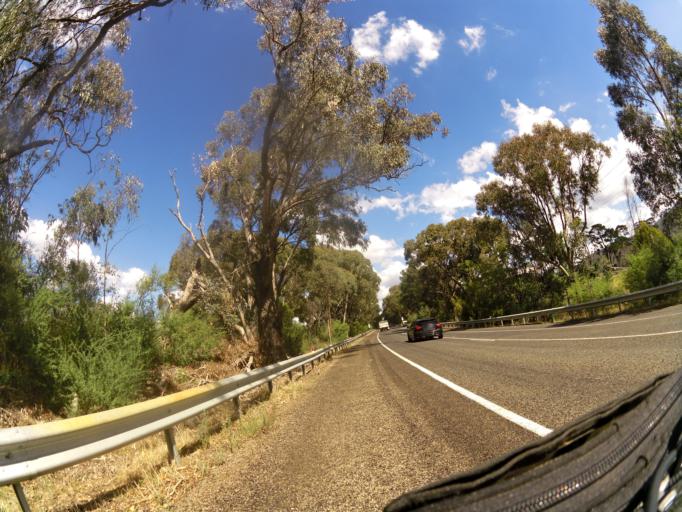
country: AU
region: Victoria
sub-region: Mansfield
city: Mansfield
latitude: -36.8302
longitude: 146.0086
